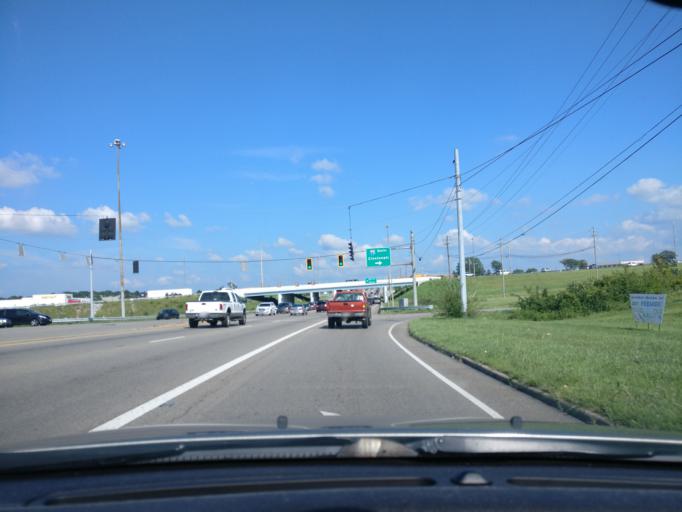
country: US
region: Ohio
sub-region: Montgomery County
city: West Carrollton City
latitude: 39.6400
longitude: -84.2342
